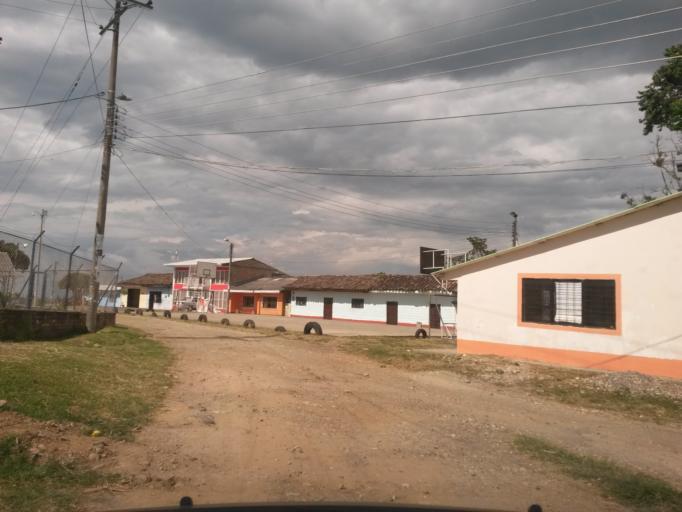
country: CO
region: Cauca
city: Rosas
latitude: 2.3462
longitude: -76.6751
